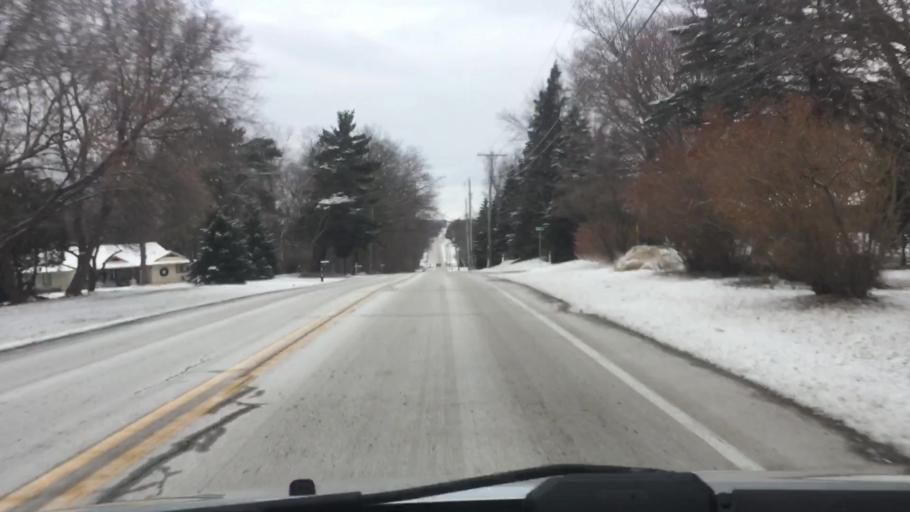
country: US
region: Wisconsin
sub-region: Waukesha County
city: Brookfield
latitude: 43.0811
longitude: -88.1059
